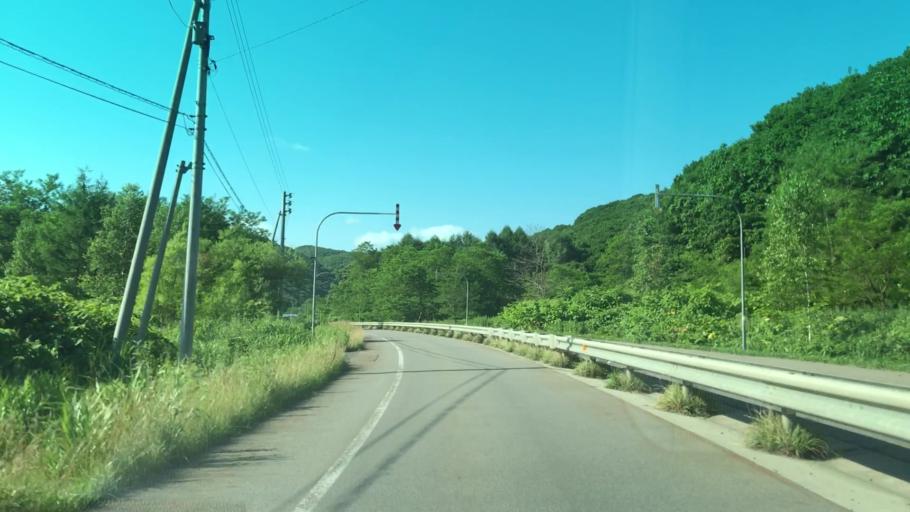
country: JP
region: Hokkaido
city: Iwanai
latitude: 43.0013
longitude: 140.6688
